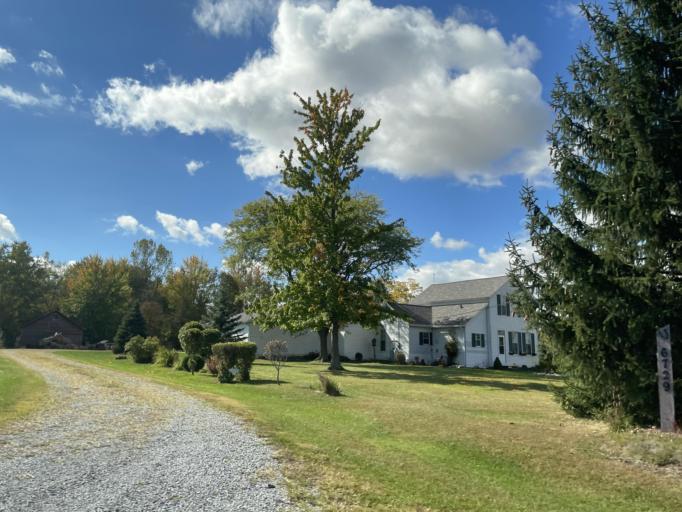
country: US
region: Indiana
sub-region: Allen County
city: Fort Wayne
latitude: 41.1158
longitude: -85.2316
